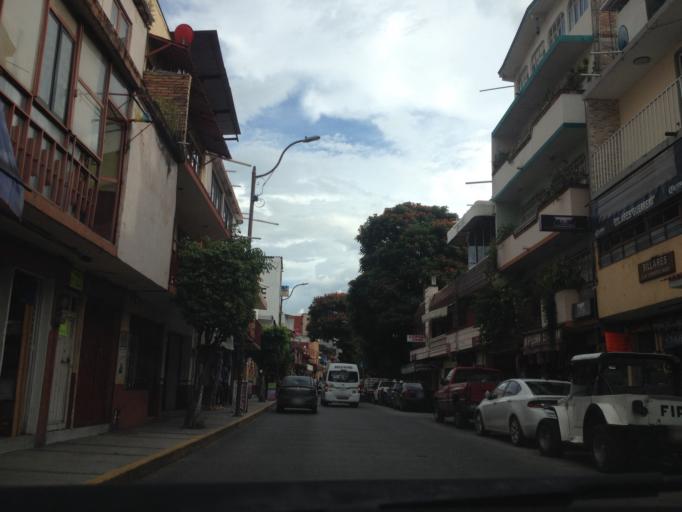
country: MX
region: Guerrero
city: Chilpancingo de los Bravos
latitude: 17.5546
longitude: -99.5037
